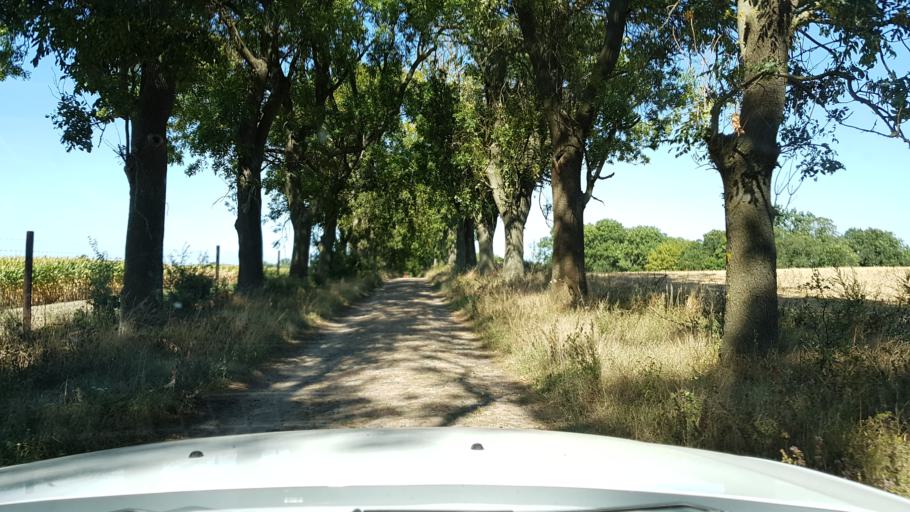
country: PL
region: West Pomeranian Voivodeship
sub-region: Powiat gryfinski
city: Cedynia
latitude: 52.8599
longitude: 14.2249
